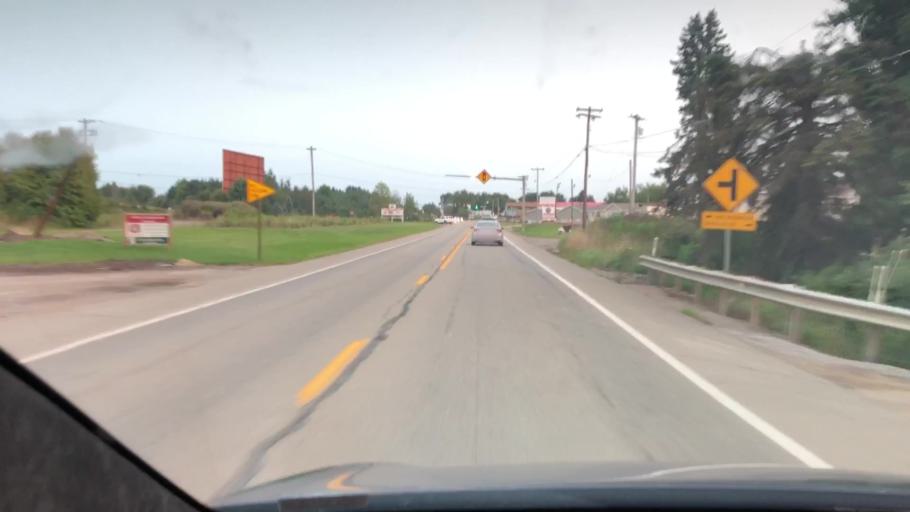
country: US
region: Pennsylvania
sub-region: Butler County
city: Shanor-Northvue
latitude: 40.9234
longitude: -79.9490
